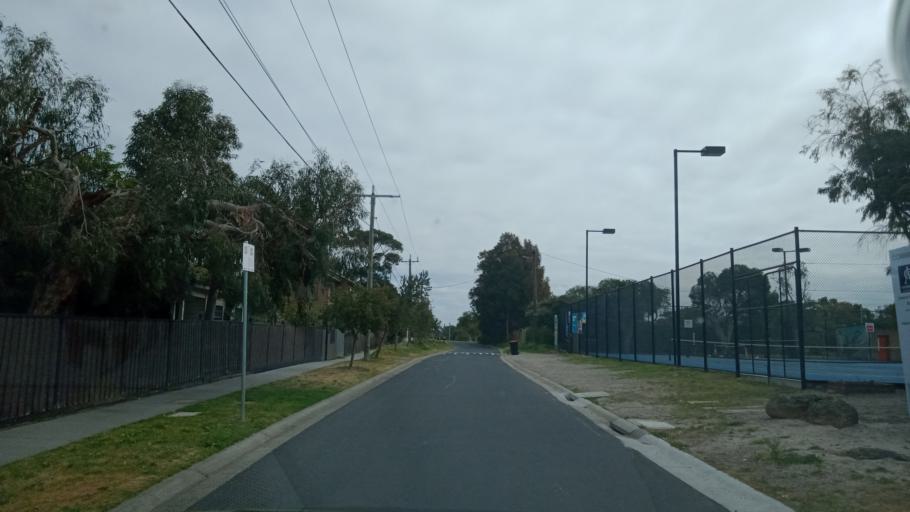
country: AU
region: Victoria
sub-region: Kingston
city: Aspendale
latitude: -38.0318
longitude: 145.1077
